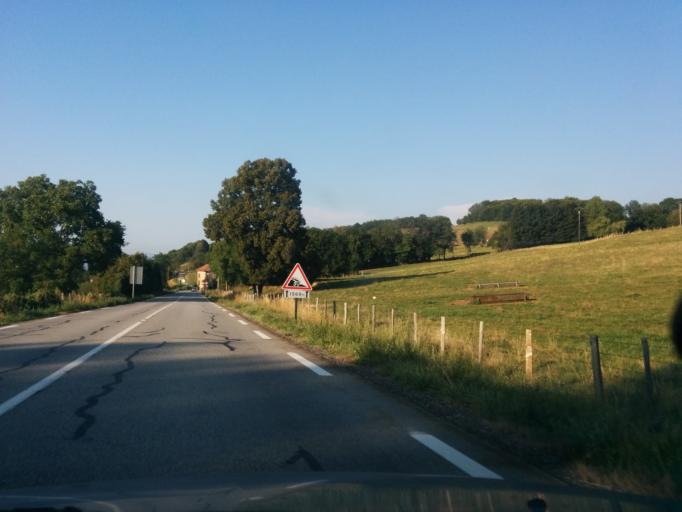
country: FR
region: Rhone-Alpes
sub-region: Departement de l'Isere
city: Montferrat
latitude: 45.4725
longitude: 5.5844
